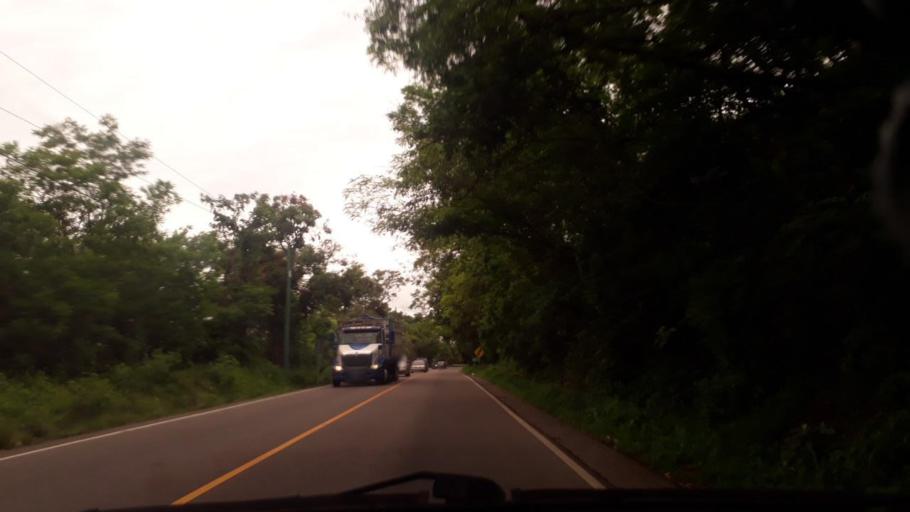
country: GT
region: Chiquimula
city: San Jacinto
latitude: 14.6500
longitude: -89.4838
